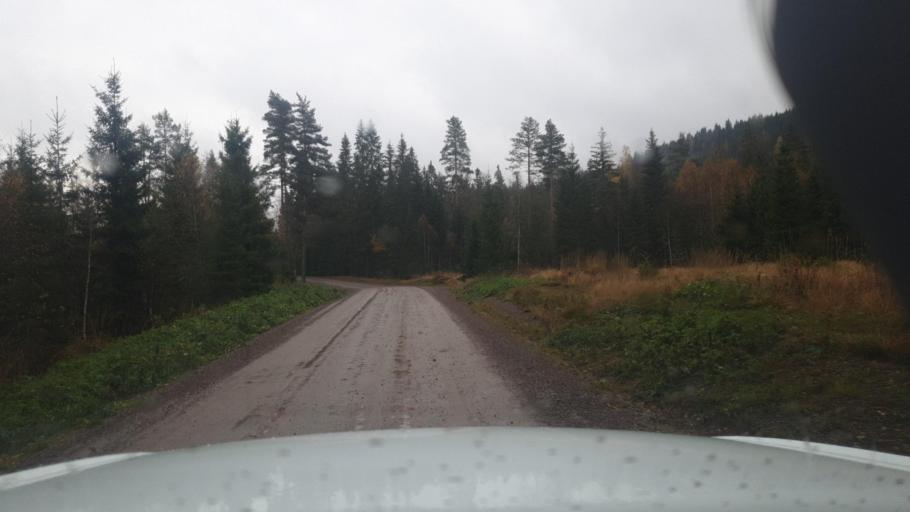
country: SE
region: Vaermland
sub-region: Eda Kommun
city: Charlottenberg
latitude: 60.0483
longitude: 12.5718
